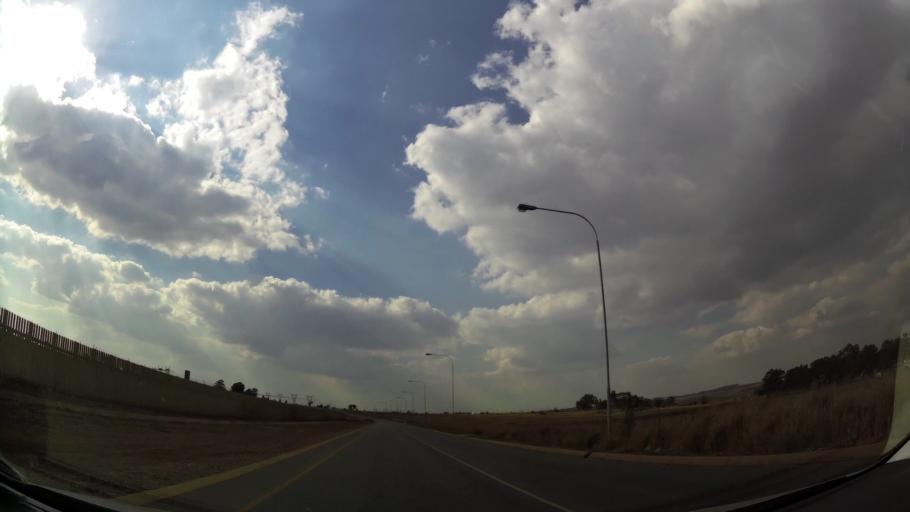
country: ZA
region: Gauteng
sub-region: City of Tshwane Metropolitan Municipality
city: Centurion
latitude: -25.9222
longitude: 28.2199
